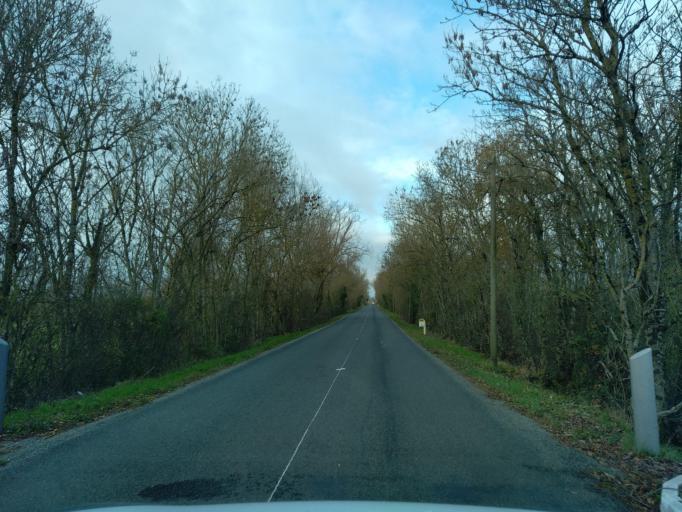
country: FR
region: Pays de la Loire
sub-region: Departement de la Vendee
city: Vix
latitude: 46.3402
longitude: -0.8268
